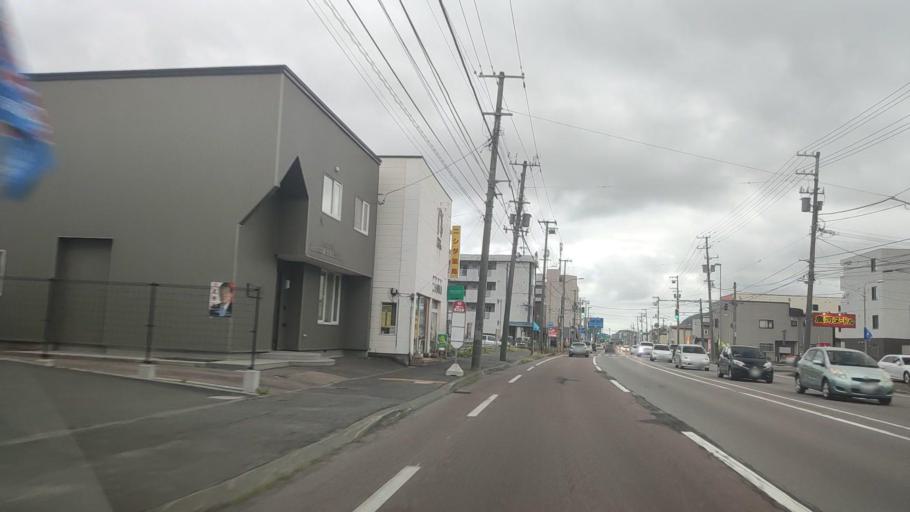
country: JP
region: Hokkaido
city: Hakodate
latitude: 41.7942
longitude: 140.7332
